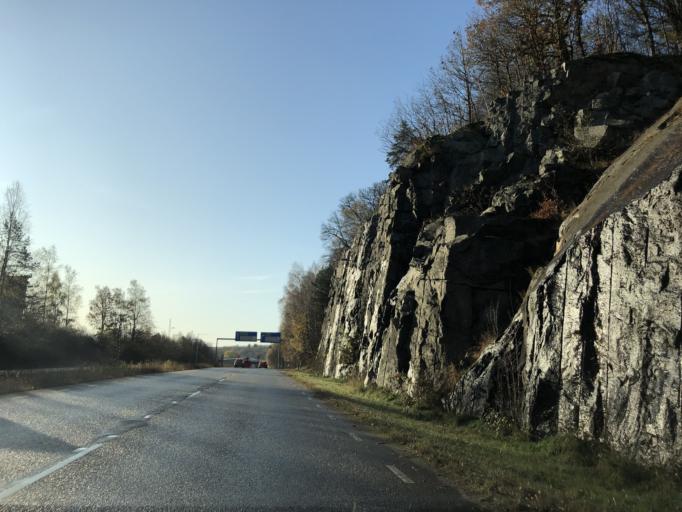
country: SE
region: Vaestra Goetaland
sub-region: Goteborg
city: Gardsten
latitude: 57.7991
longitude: 12.0421
